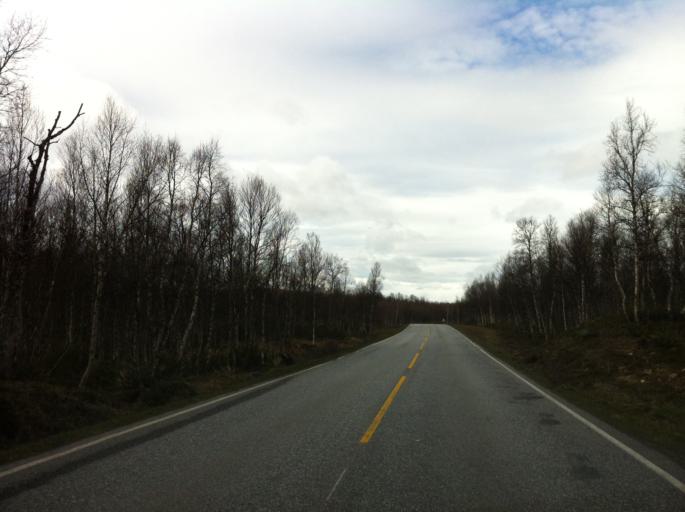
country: NO
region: Sor-Trondelag
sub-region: Roros
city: Roros
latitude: 62.5989
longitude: 11.6879
